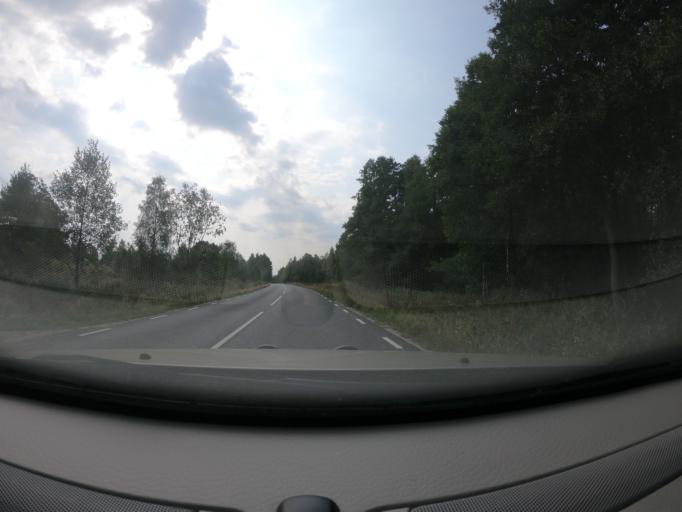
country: SE
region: Kronoberg
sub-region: Vaxjo Kommun
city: Braas
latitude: 57.1655
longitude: 14.9601
